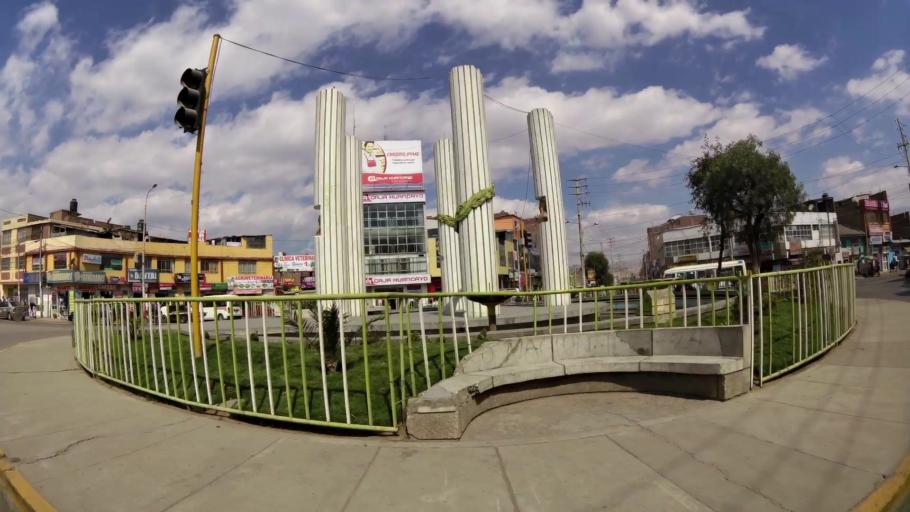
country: PE
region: Junin
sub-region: Provincia de Huancayo
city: El Tambo
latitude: -12.0861
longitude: -75.2083
